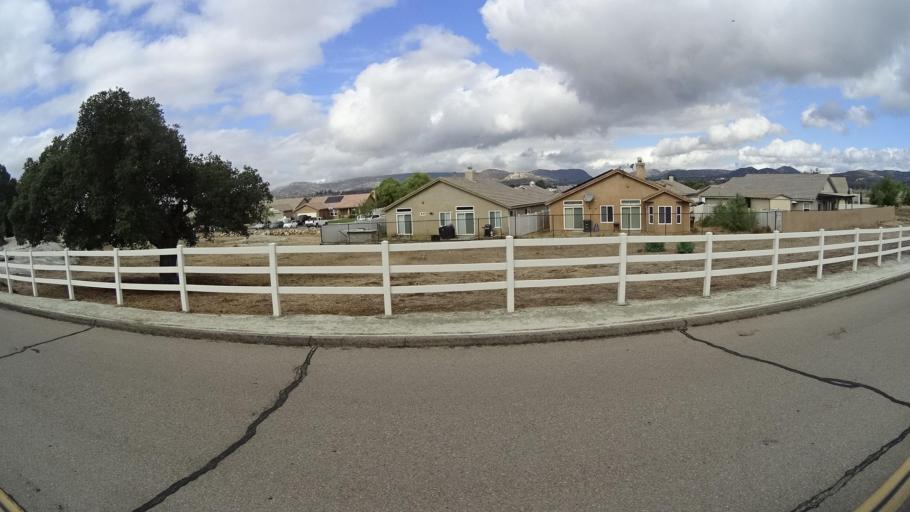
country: US
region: California
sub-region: San Diego County
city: Campo
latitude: 32.6235
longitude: -116.4630
